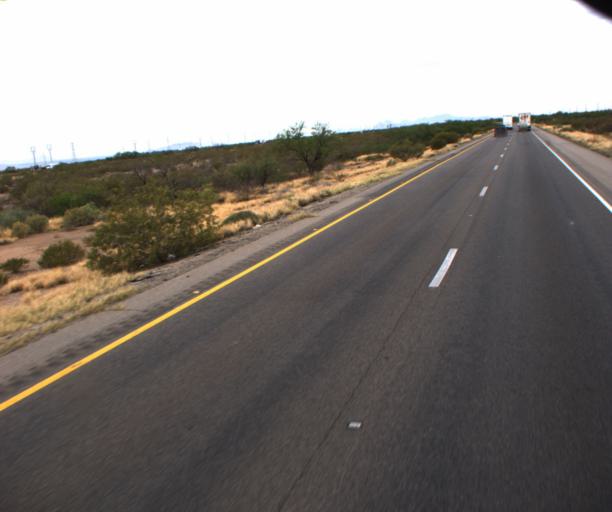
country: US
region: Arizona
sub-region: Pima County
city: Vail
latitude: 32.0392
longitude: -110.7354
